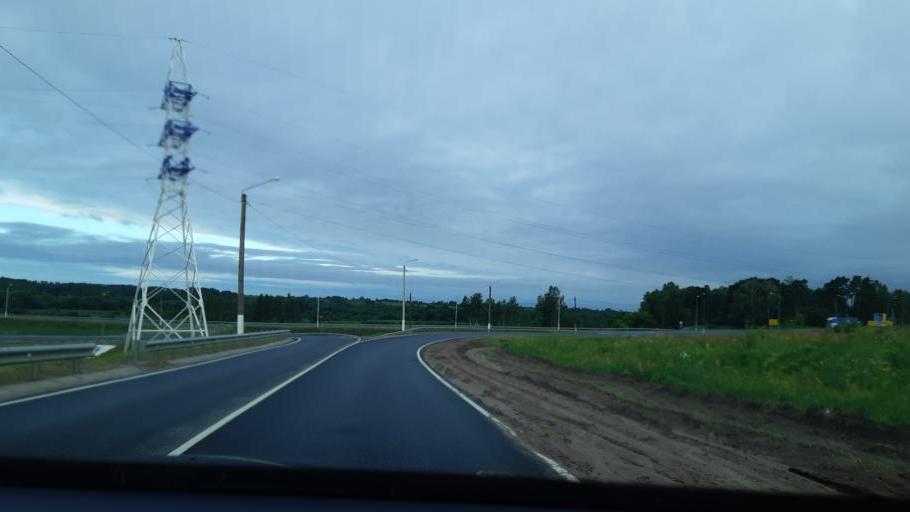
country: RU
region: Smolensk
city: Oster
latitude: 53.9829
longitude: 32.8283
